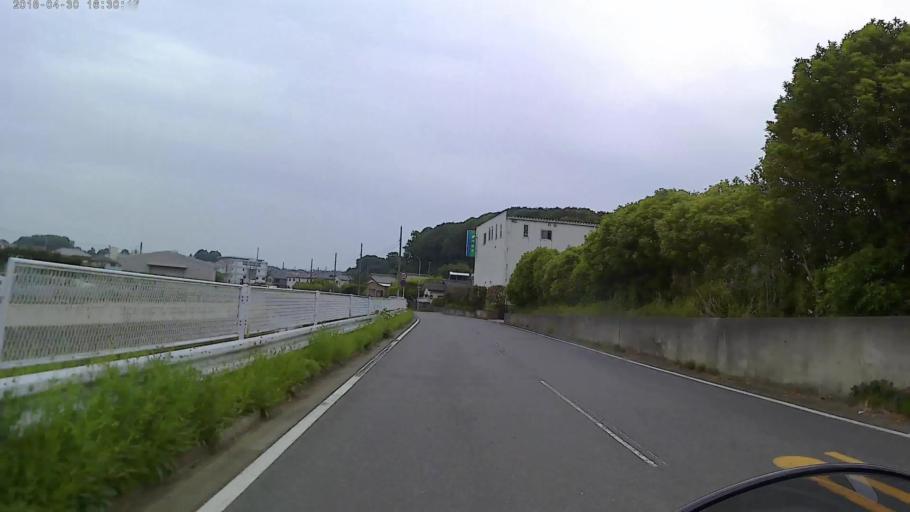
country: JP
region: Kanagawa
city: Zama
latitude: 35.4551
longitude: 139.4040
